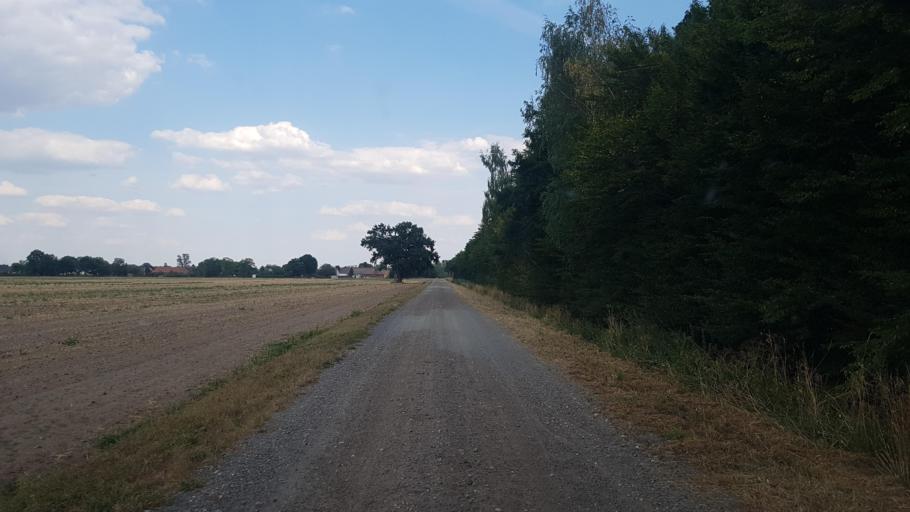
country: DE
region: Brandenburg
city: Herzberg
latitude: 51.6821
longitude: 13.2651
